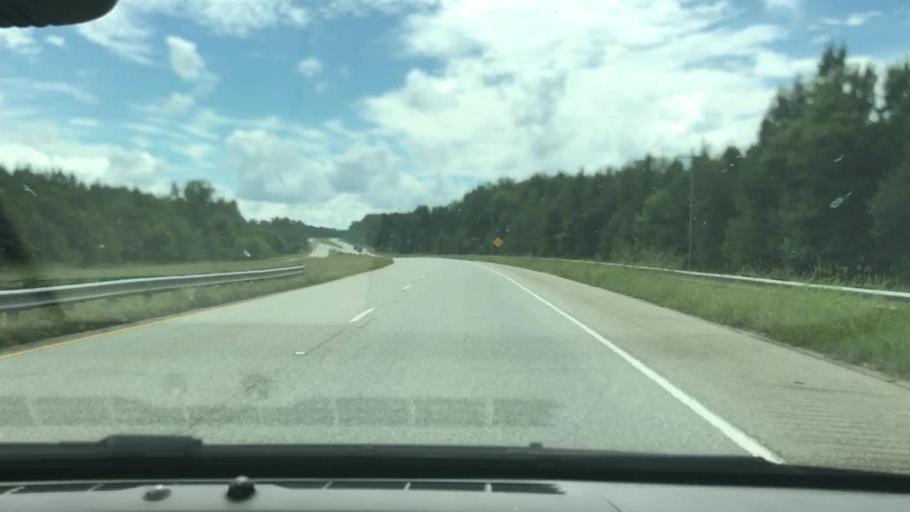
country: US
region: Georgia
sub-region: Stewart County
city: Lumpkin
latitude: 32.1540
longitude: -84.8283
